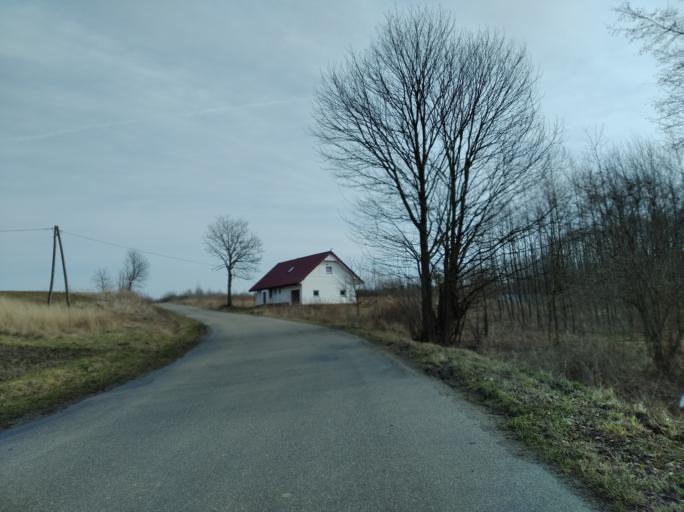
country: PL
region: Subcarpathian Voivodeship
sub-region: Powiat brzozowski
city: Stara Wies
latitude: 49.7160
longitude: 21.9765
